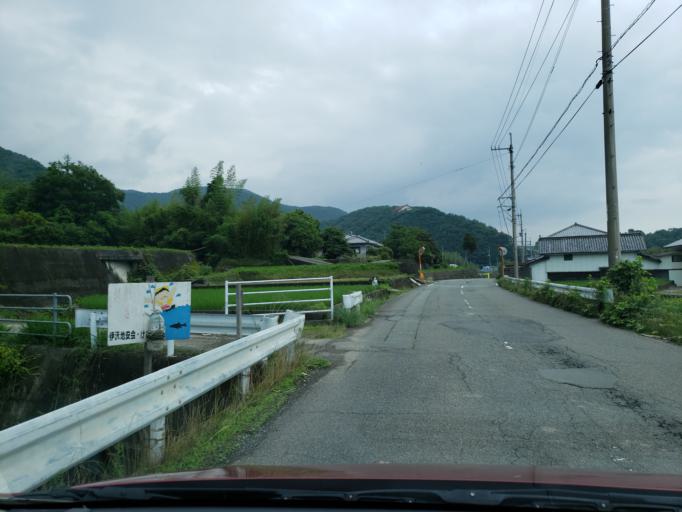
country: JP
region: Tokushima
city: Wakimachi
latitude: 34.1033
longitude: 134.2340
